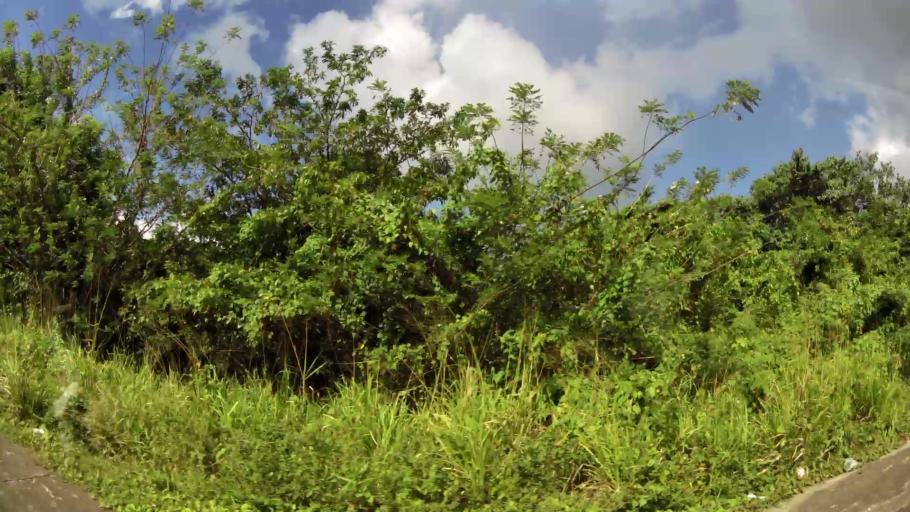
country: MQ
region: Martinique
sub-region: Martinique
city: Les Trois-Ilets
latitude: 14.5342
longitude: -61.0280
